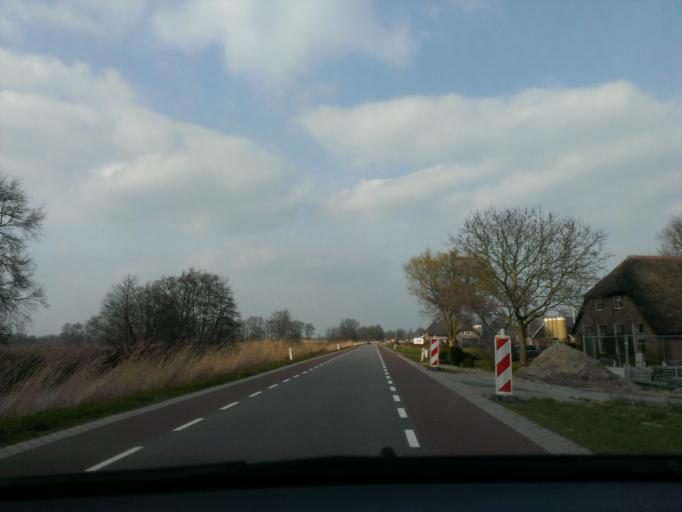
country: NL
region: Gelderland
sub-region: Gemeente Epe
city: Vaassen
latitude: 52.2507
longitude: 5.9801
